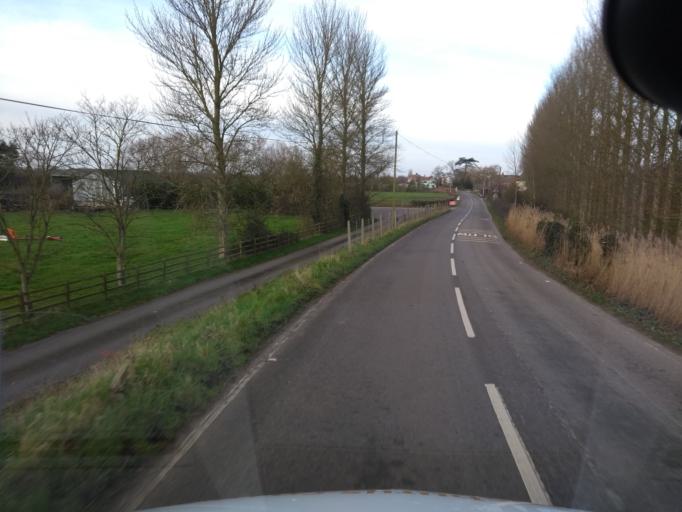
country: GB
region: England
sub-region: Somerset
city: Burnham-on-Sea
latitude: 51.2586
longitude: -2.9711
